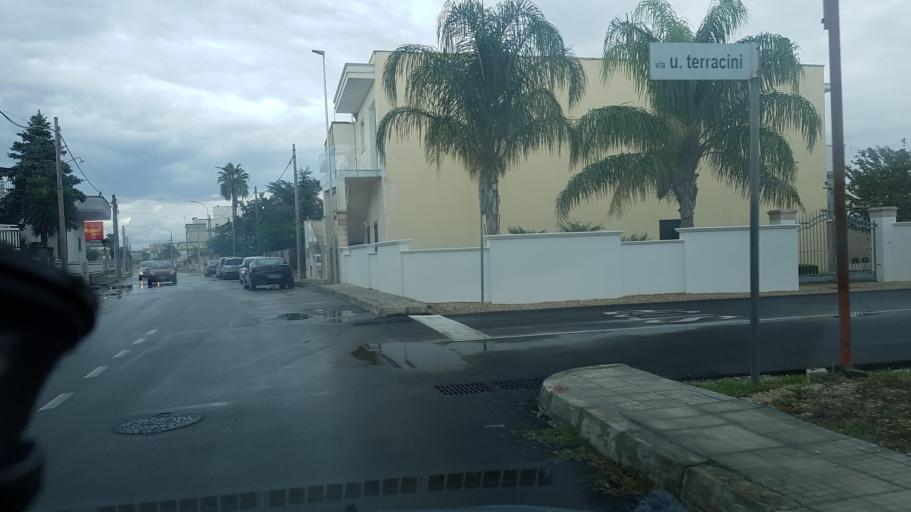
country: IT
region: Apulia
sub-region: Provincia di Lecce
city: Salice Salentino
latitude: 40.3905
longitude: 17.9592
